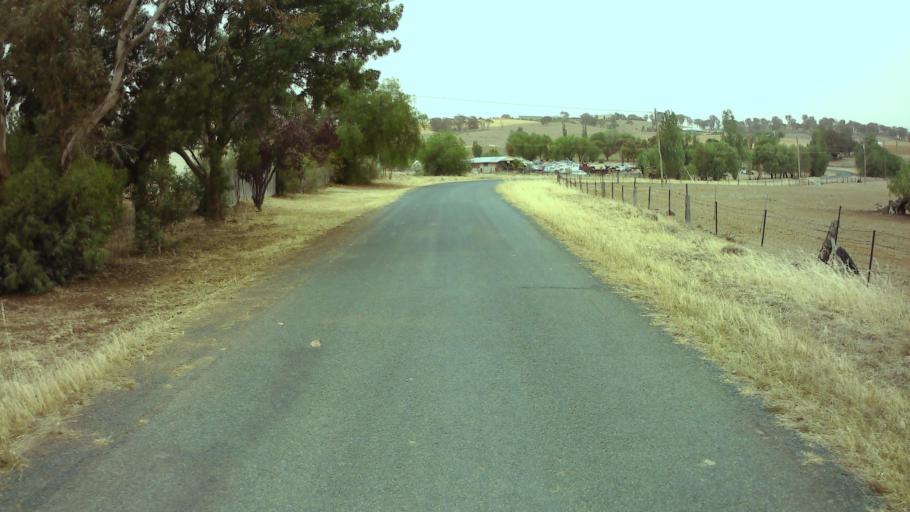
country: AU
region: New South Wales
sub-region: Weddin
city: Grenfell
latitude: -33.9050
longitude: 148.1697
